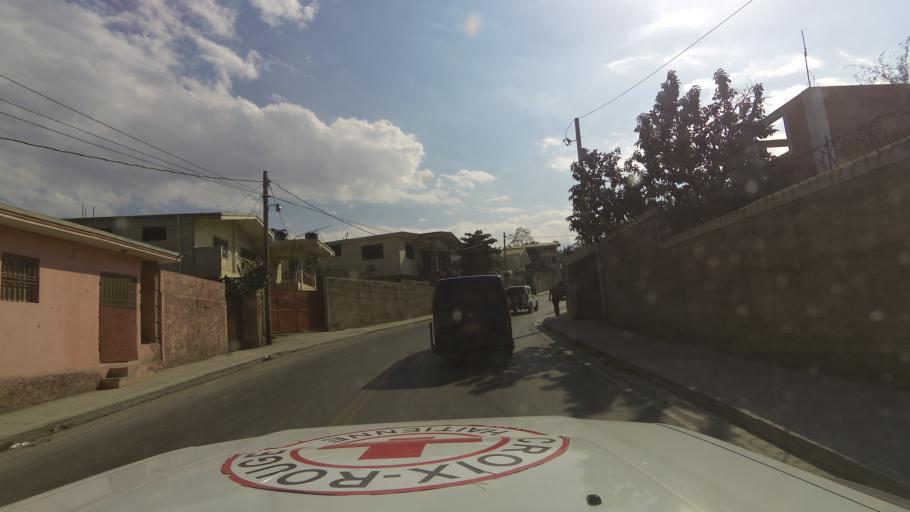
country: HT
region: Ouest
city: Delmas 73
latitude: 18.5352
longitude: -72.2871
